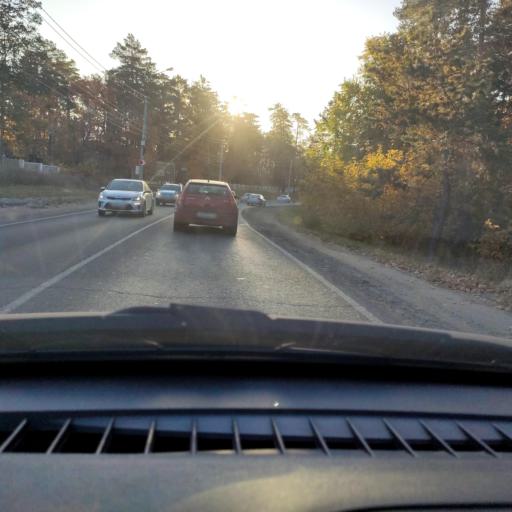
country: RU
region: Samara
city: Tol'yatti
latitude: 53.4861
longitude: 49.3134
